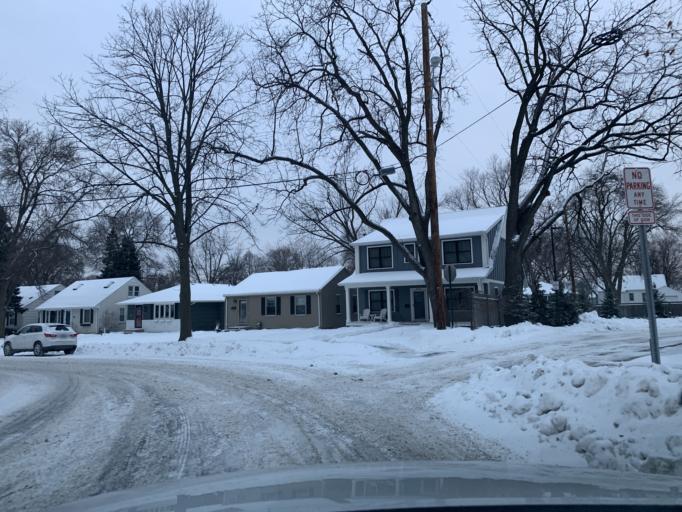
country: US
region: Minnesota
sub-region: Hennepin County
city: Saint Louis Park
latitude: 44.9288
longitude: -93.3469
